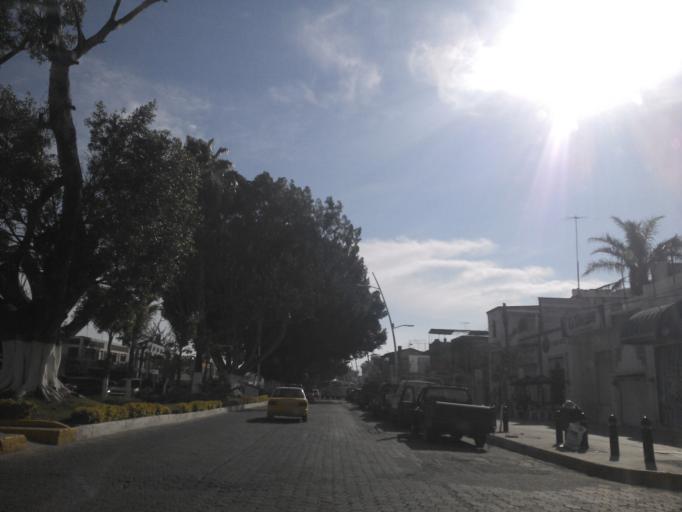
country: MX
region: Jalisco
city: Chapala
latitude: 20.2952
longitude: -103.1910
